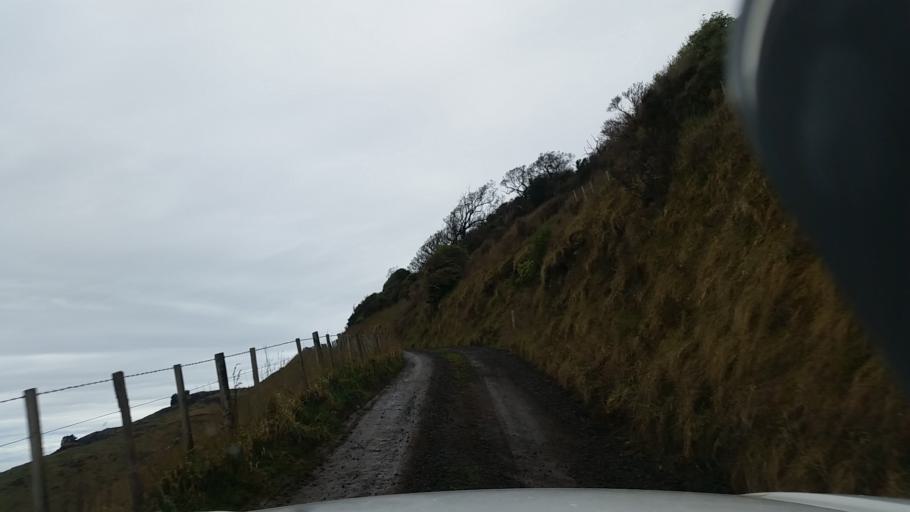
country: NZ
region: Canterbury
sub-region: Christchurch City
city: Christchurch
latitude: -43.7443
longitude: 172.9996
